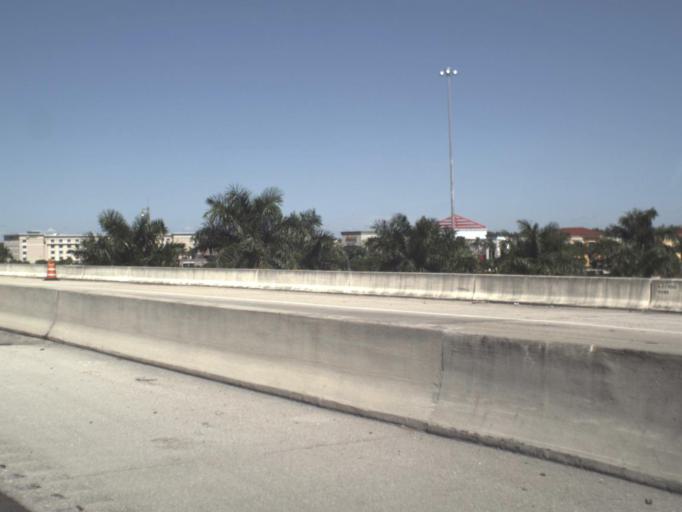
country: US
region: Florida
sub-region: Lee County
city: Three Oaks
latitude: 26.4926
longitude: -81.7942
